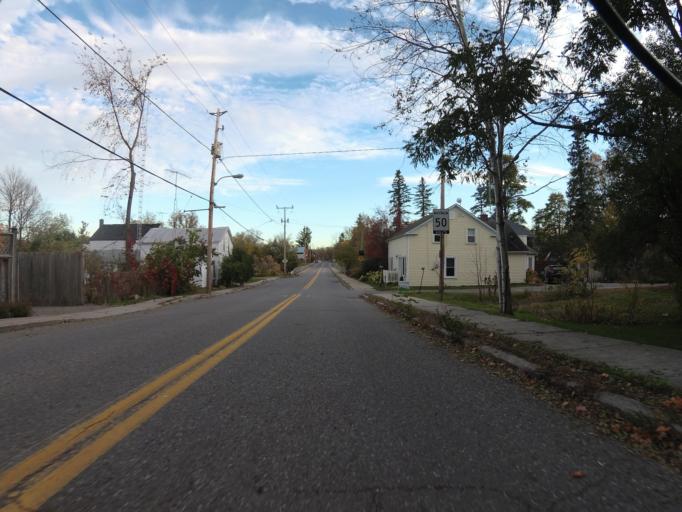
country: CA
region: Ontario
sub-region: Lanark County
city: Smiths Falls
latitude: 44.9818
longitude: -75.7948
